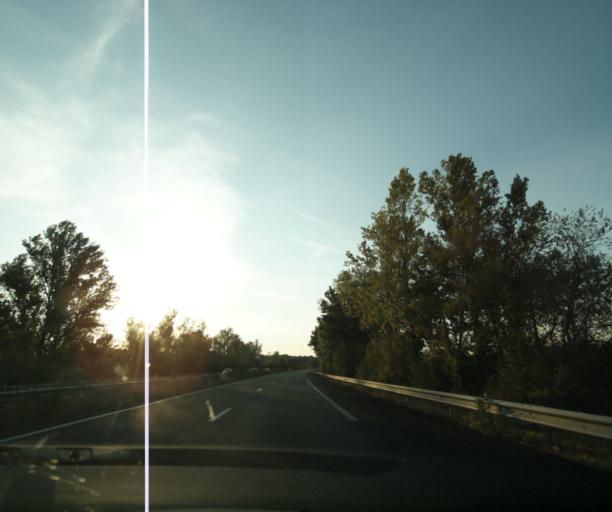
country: FR
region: Aquitaine
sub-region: Departement du Lot-et-Garonne
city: Castelculier
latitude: 44.1094
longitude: 0.7382
